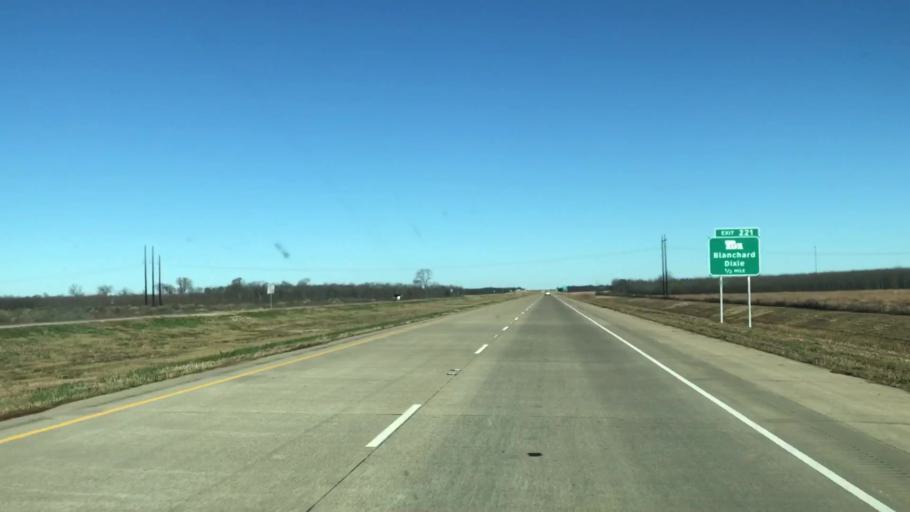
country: US
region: Louisiana
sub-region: Caddo Parish
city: Blanchard
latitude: 32.6633
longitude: -93.8453
